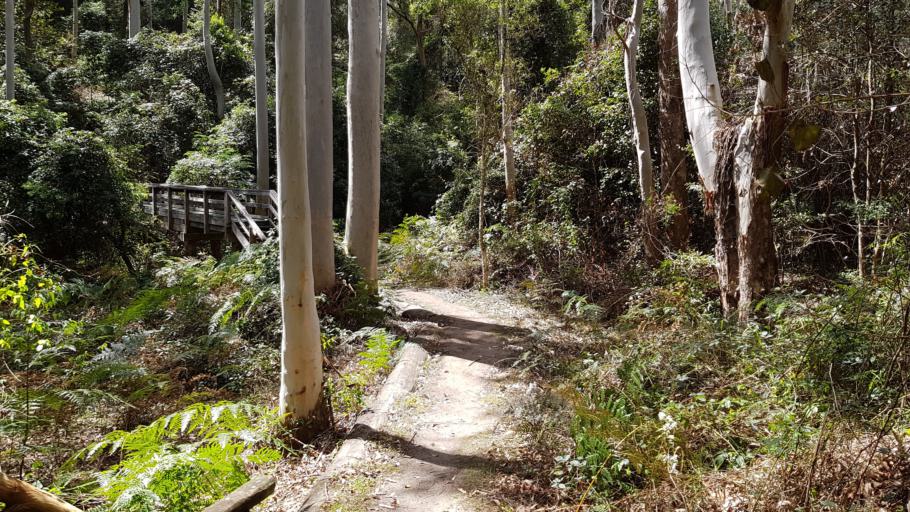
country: AU
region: New South Wales
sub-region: Hornsby Shire
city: Glenorie
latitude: -33.4007
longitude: 151.0487
